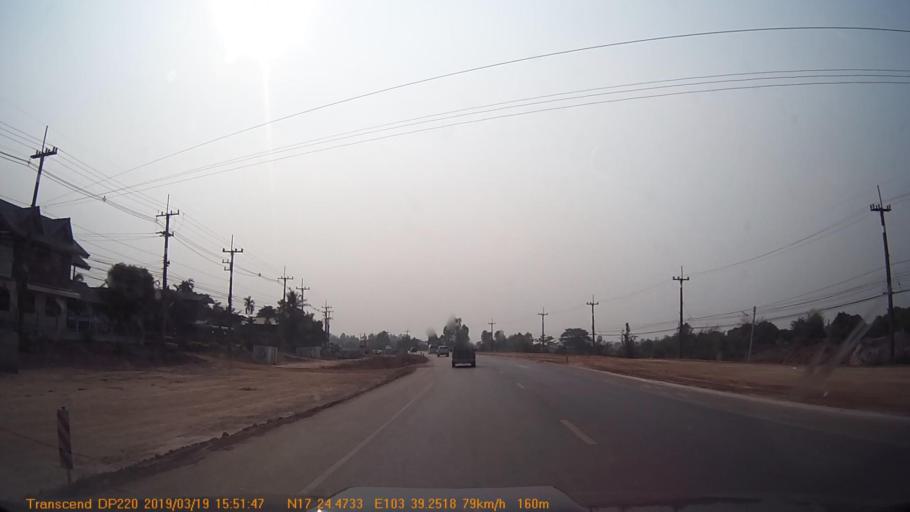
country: TH
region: Sakon Nakhon
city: Phang Khon
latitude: 17.4080
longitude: 103.6538
